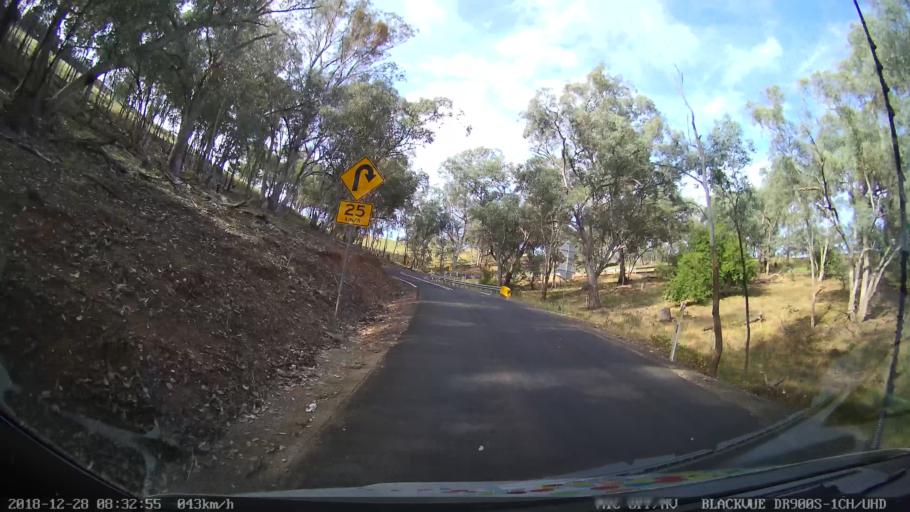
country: AU
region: New South Wales
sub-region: Blayney
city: Blayney
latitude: -33.9646
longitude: 149.3106
